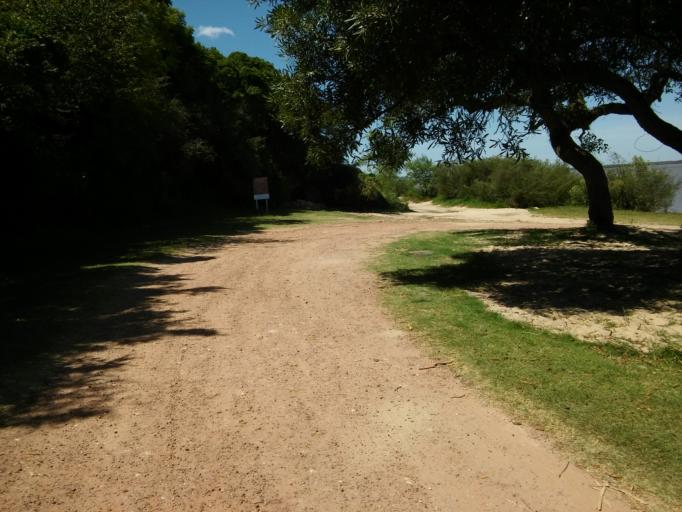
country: UY
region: Colonia
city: Nueva Palmira
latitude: -33.9161
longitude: -58.4153
